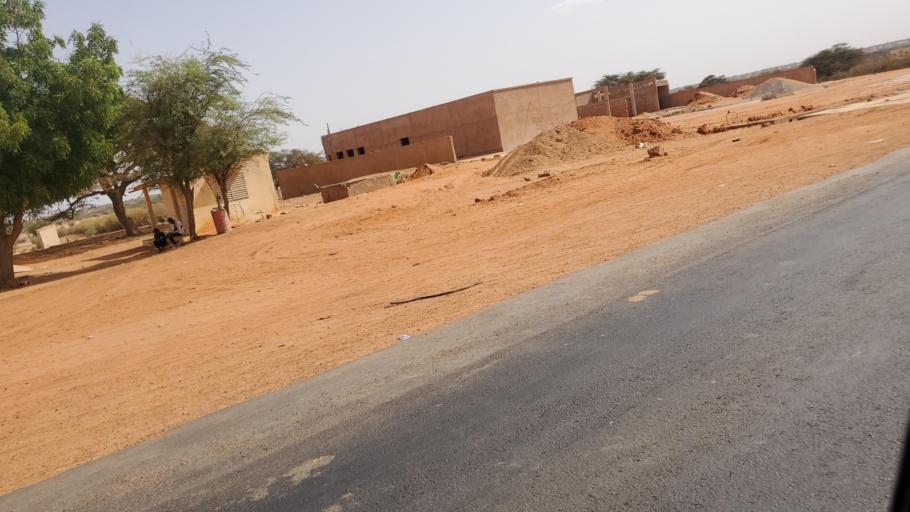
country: SN
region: Louga
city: Ndibene Dahra
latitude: 15.3985
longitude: -15.1316
